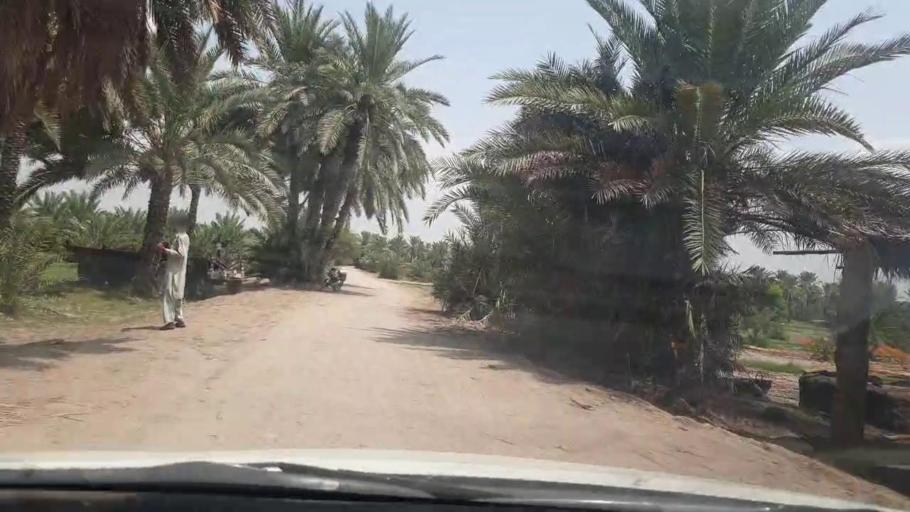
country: PK
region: Sindh
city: Khairpur
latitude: 27.5507
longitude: 68.8316
